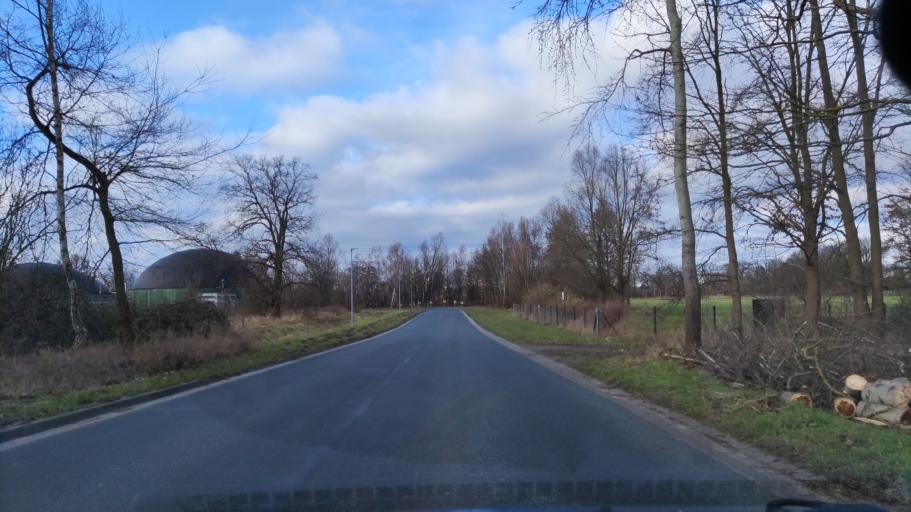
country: DE
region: Lower Saxony
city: Dannenberg
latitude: 53.1054
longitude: 11.1303
